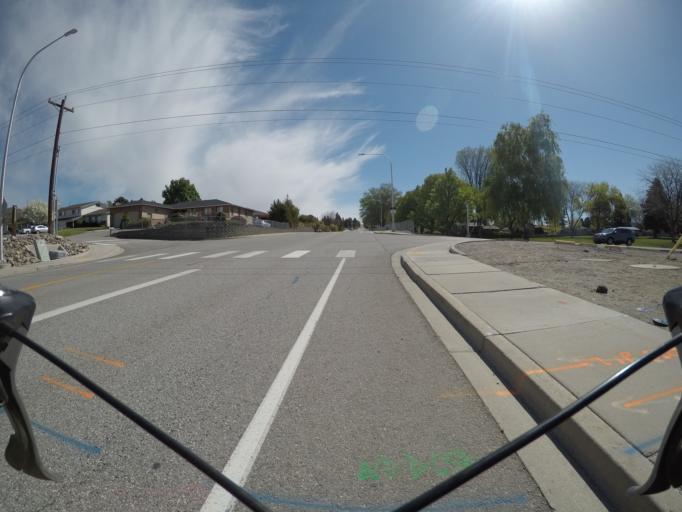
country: US
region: Washington
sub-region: Douglas County
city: East Wenatchee Bench
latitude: 47.4166
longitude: -120.2697
